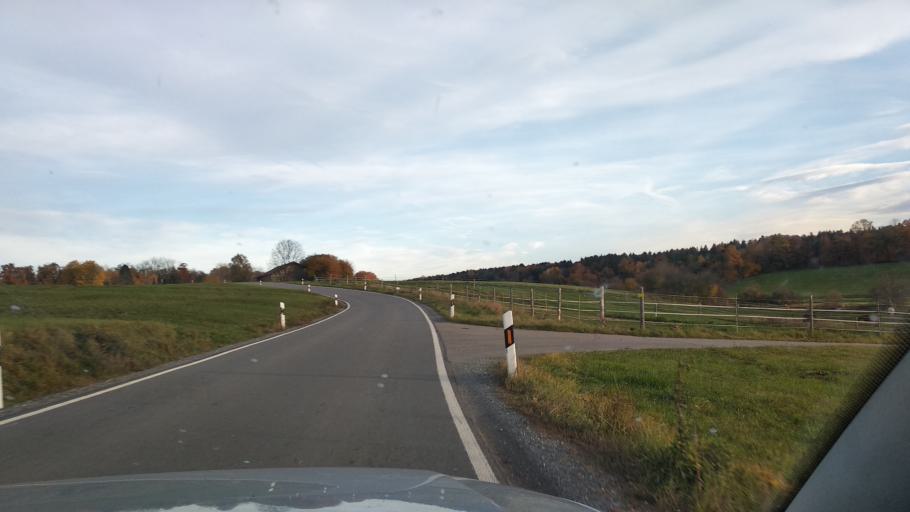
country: DE
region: Bavaria
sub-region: Upper Bavaria
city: Bruck
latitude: 48.0402
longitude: 11.9272
